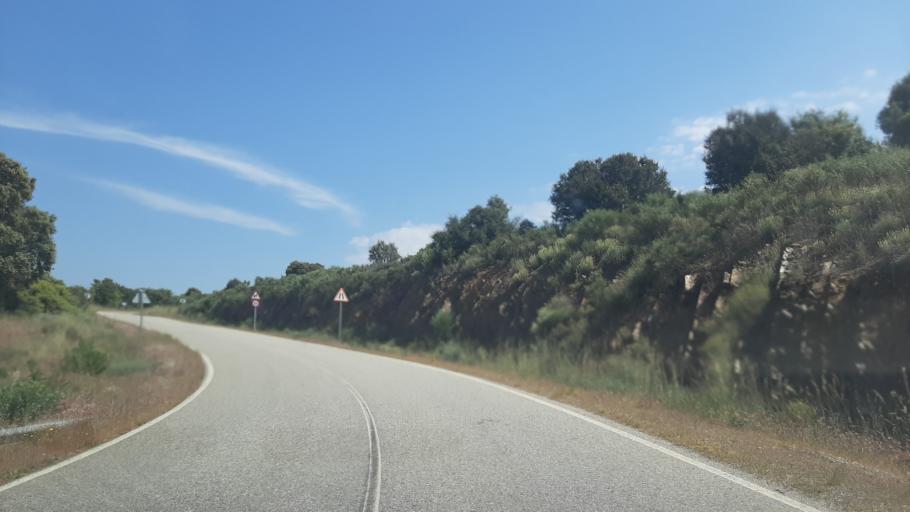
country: ES
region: Castille and Leon
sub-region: Provincia de Salamanca
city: Aldea del Obispo
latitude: 40.6532
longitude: -6.7770
